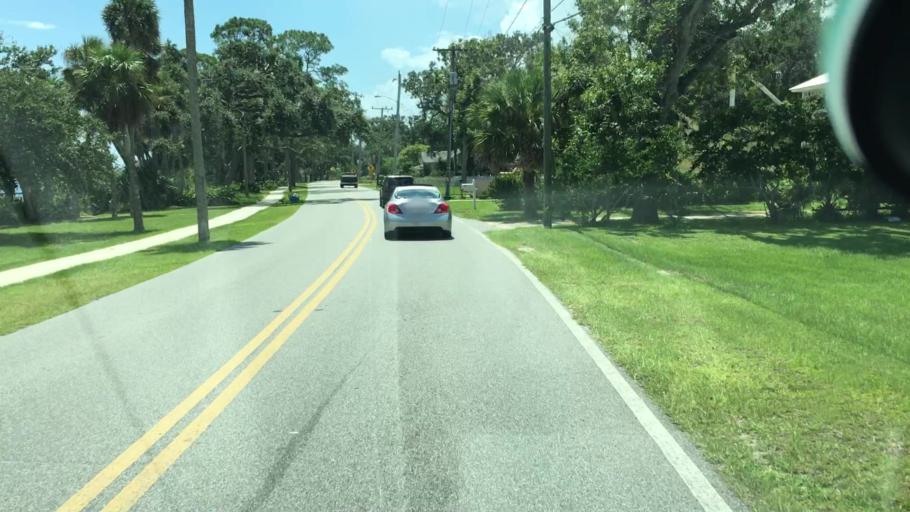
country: US
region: Florida
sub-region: Volusia County
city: Holly Hill
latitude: 29.2544
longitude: -81.0396
